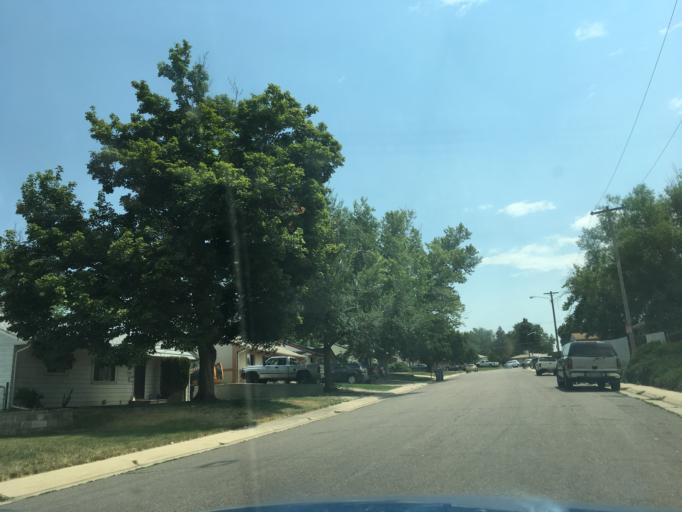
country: US
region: Colorado
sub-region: Arapahoe County
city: Sheridan
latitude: 39.6836
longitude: -105.0391
